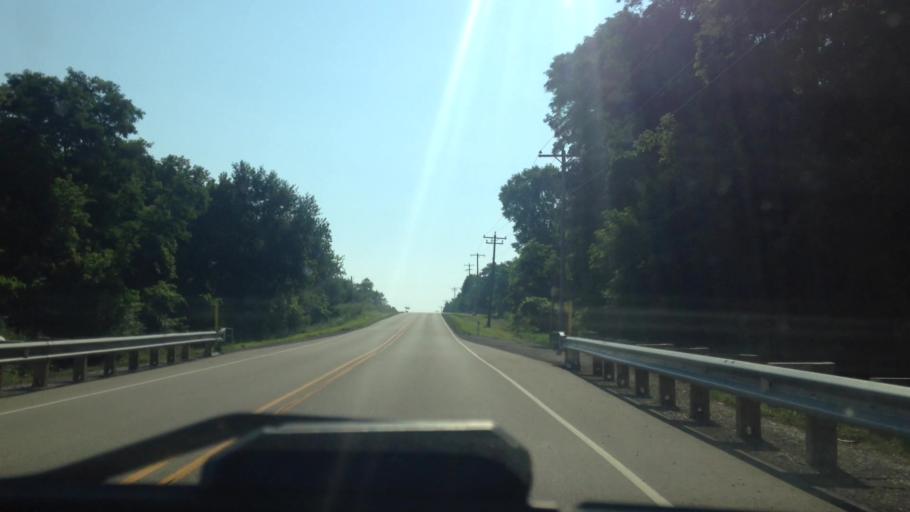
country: US
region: Wisconsin
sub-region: Waukesha County
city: Merton
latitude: 43.1630
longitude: -88.2859
